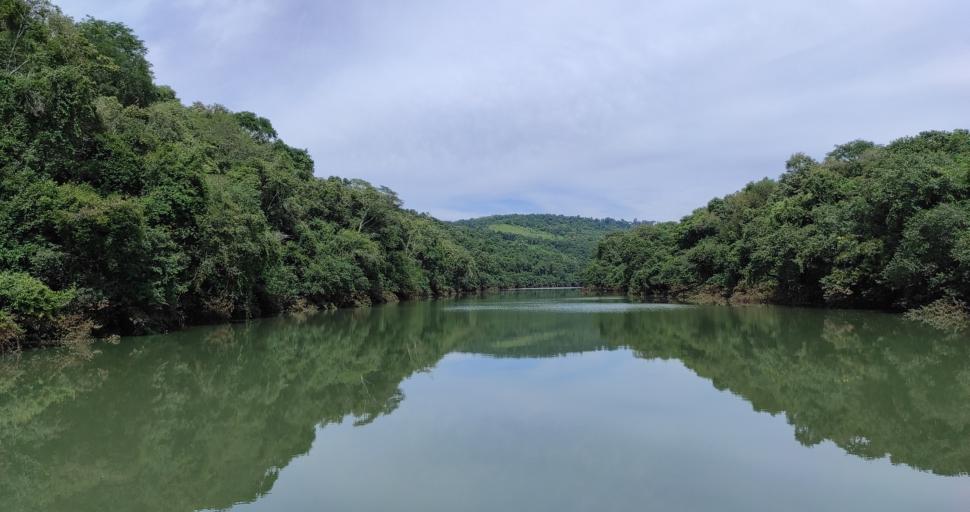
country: AR
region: Misiones
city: El Soberbio
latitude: -27.2821
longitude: -54.2023
